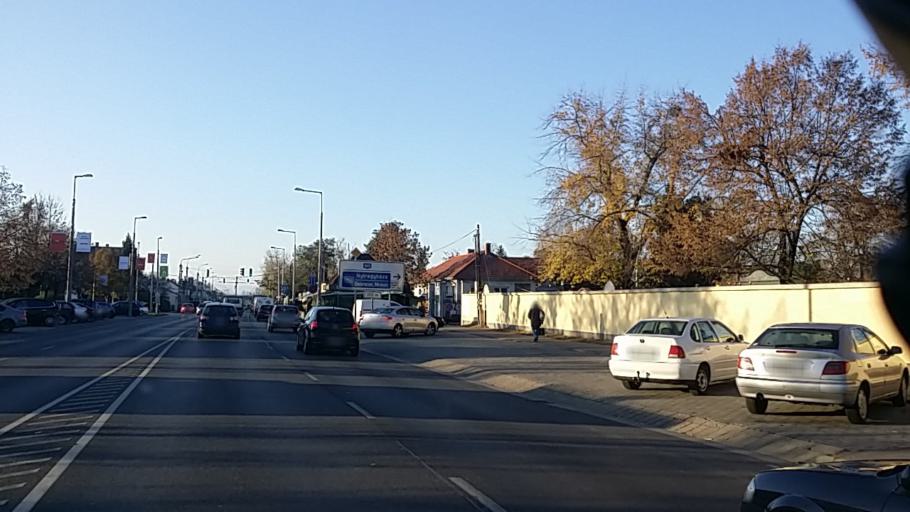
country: HU
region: Budapest
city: Budapest XV. keruelet
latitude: 47.5515
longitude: 19.1355
